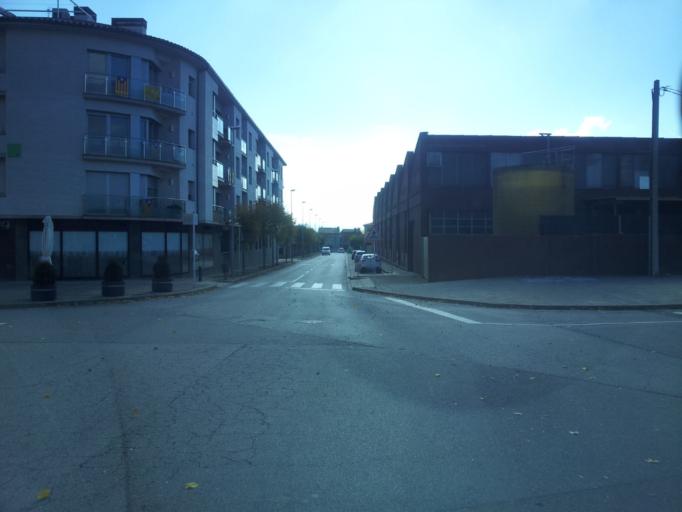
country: ES
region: Catalonia
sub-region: Provincia de Barcelona
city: Vic
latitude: 41.9293
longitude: 2.2431
